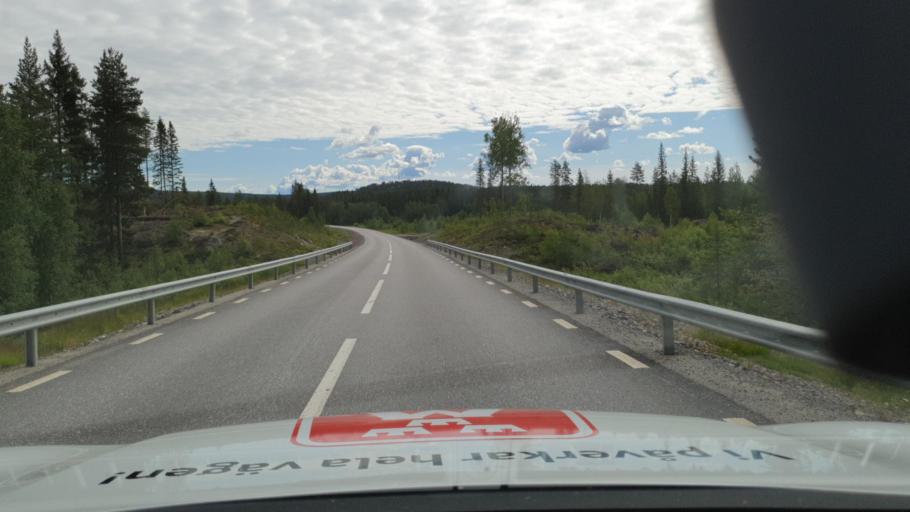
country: SE
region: Vaesterbotten
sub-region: Umea Kommun
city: Ersmark
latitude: 64.2577
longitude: 20.2027
